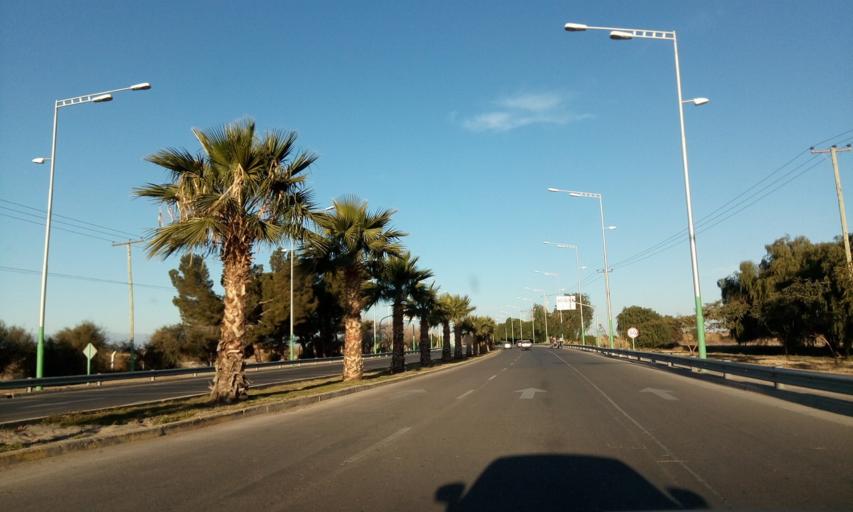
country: AR
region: San Juan
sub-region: Departamento de Rivadavia
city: Rivadavia
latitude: -31.5239
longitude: -68.6160
